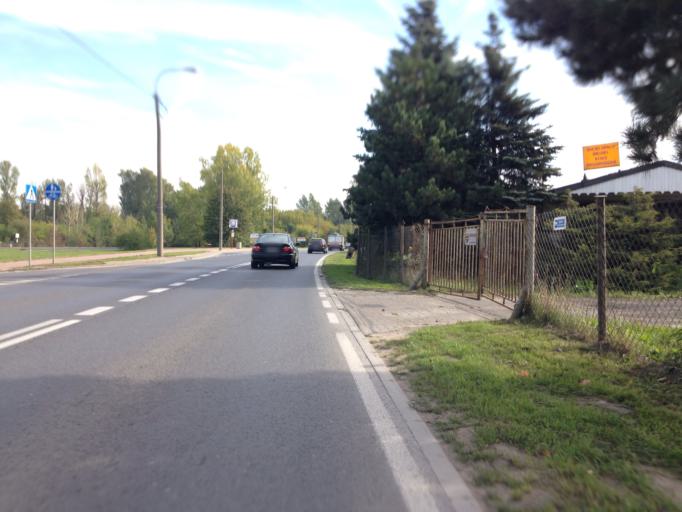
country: PL
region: Masovian Voivodeship
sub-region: Warszawa
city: Praga Poludnie
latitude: 52.2606
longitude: 21.0866
